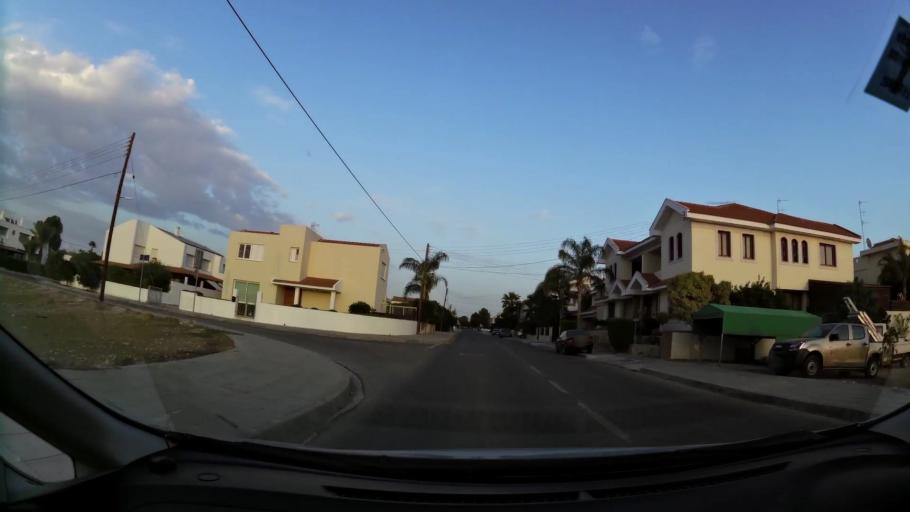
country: CY
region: Lefkosia
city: Nicosia
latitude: 35.1597
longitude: 33.3261
